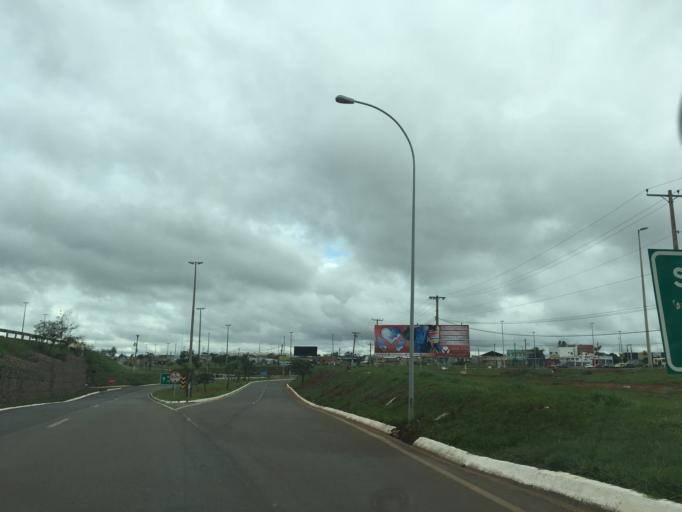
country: BR
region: Federal District
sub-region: Brasilia
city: Brasilia
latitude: -16.0013
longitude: -47.9847
